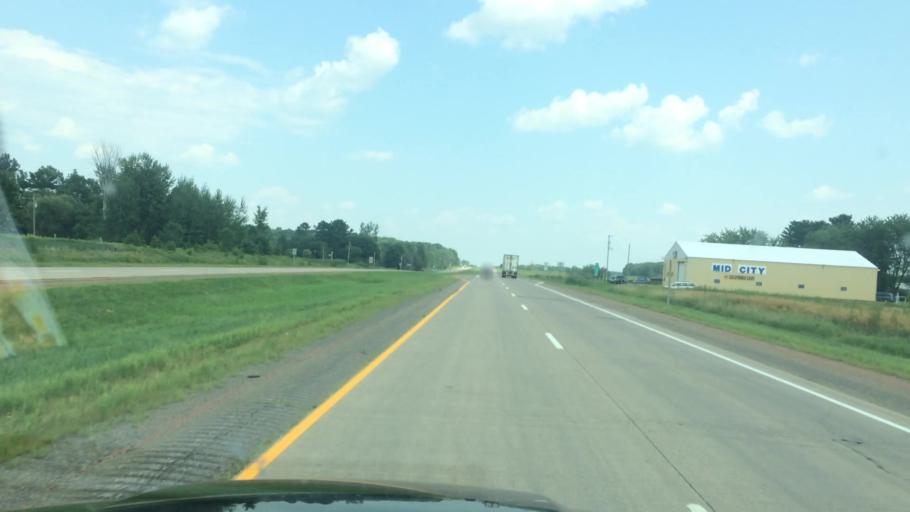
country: US
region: Wisconsin
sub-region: Marathon County
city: Athens
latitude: 44.9452
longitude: -90.1429
